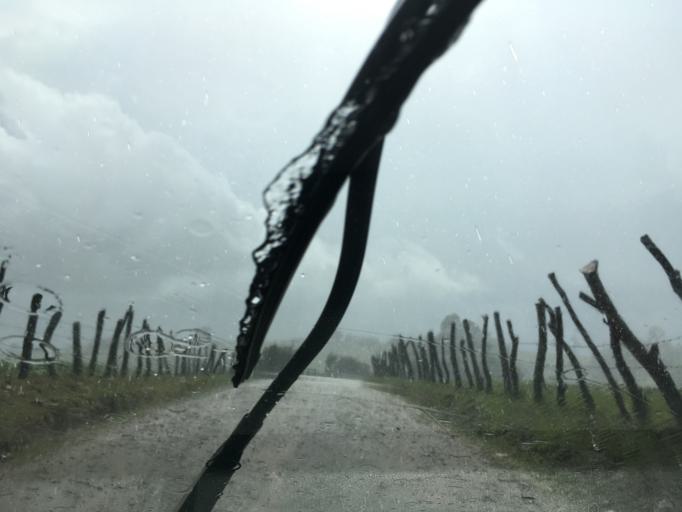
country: MX
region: Michoacan
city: Acuitzio del Canje
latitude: 19.5269
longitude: -101.2260
